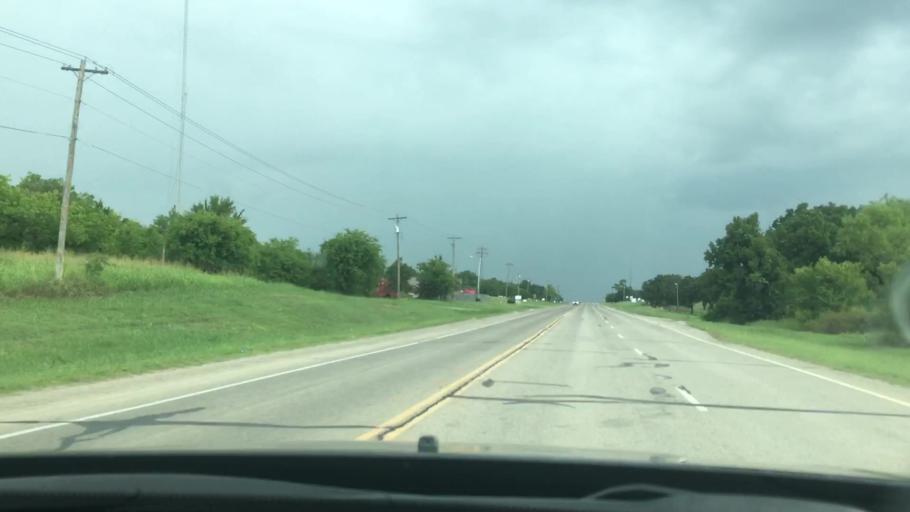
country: US
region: Oklahoma
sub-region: Carter County
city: Healdton
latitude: 34.2115
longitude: -97.4748
